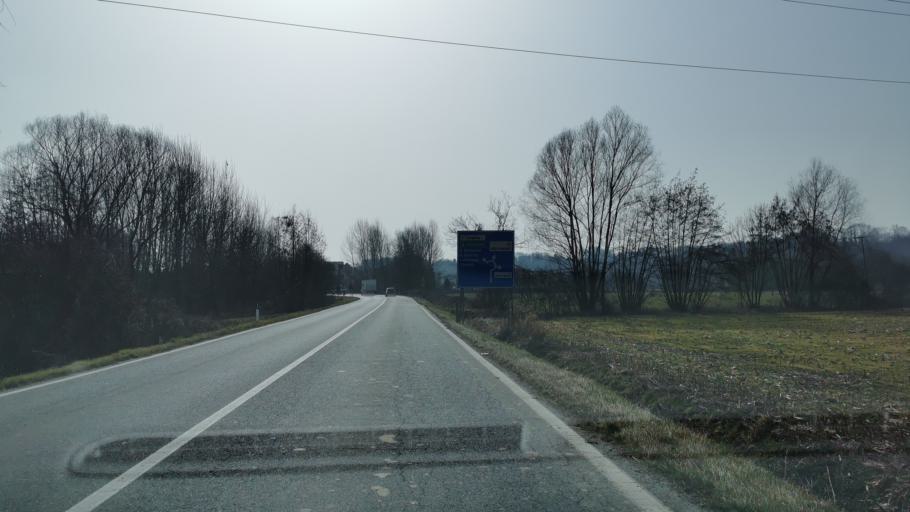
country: IT
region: Piedmont
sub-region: Provincia di Torino
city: Volpiano
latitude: 45.2126
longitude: 7.7733
